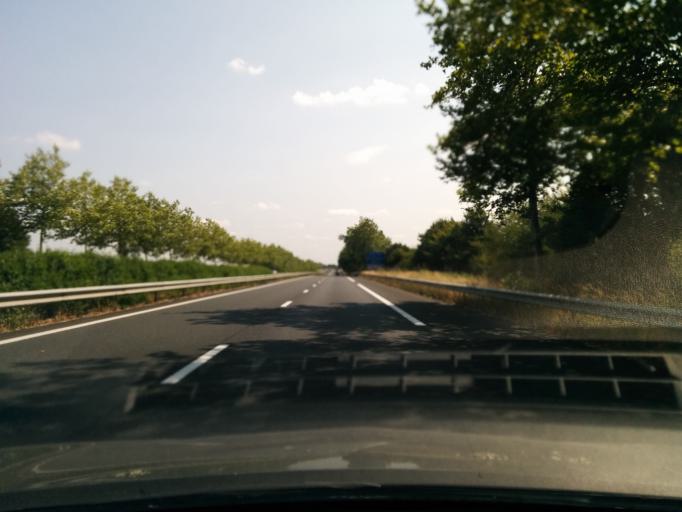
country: FR
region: Centre
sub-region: Departement de l'Indre
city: Montierchaume
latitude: 46.8980
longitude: 1.7319
